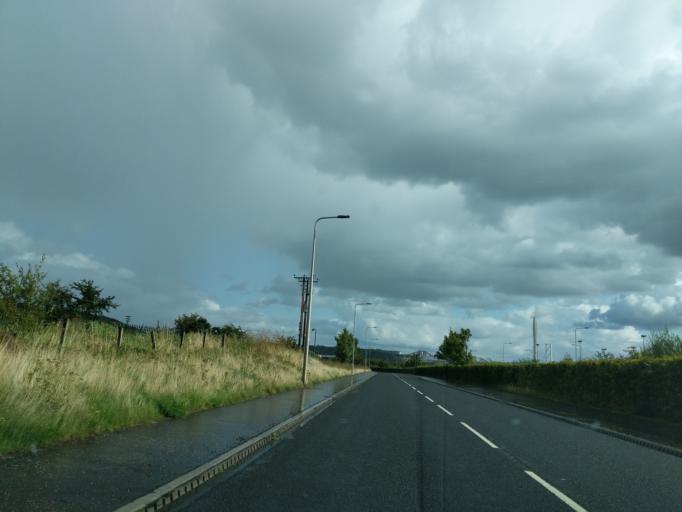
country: GB
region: Scotland
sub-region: Fife
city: Rosyth
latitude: 56.0235
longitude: -3.4280
